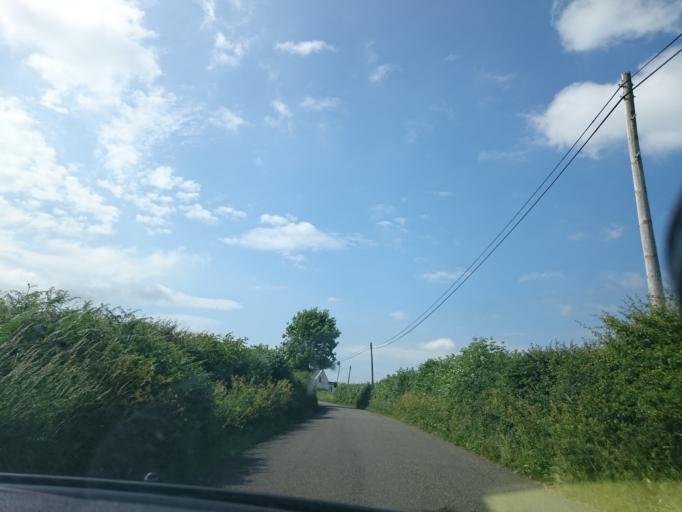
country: IE
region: Leinster
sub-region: Kilkenny
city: Thomastown
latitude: 52.5233
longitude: -7.1996
